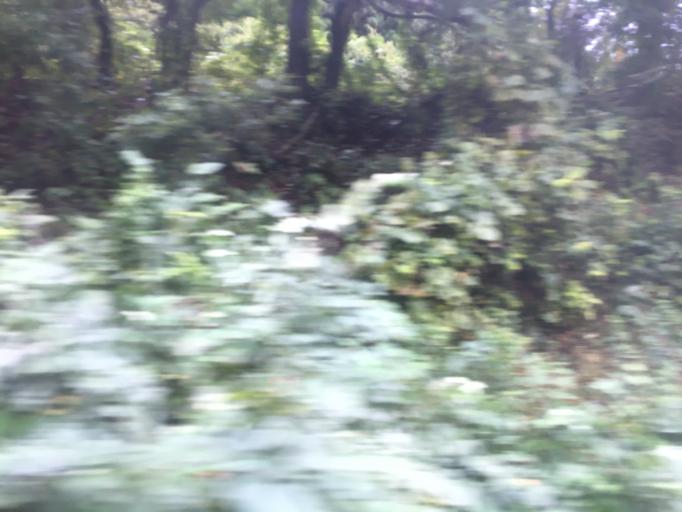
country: JP
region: Niigata
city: Murakami
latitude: 38.0767
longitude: 139.6631
